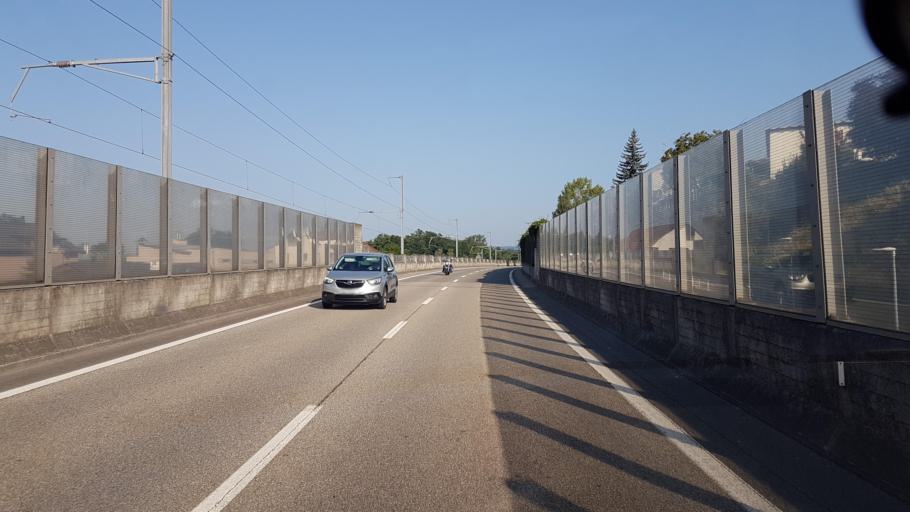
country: CH
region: Aargau
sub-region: Bezirk Zurzach
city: Klingnau
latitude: 47.5827
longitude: 8.2470
